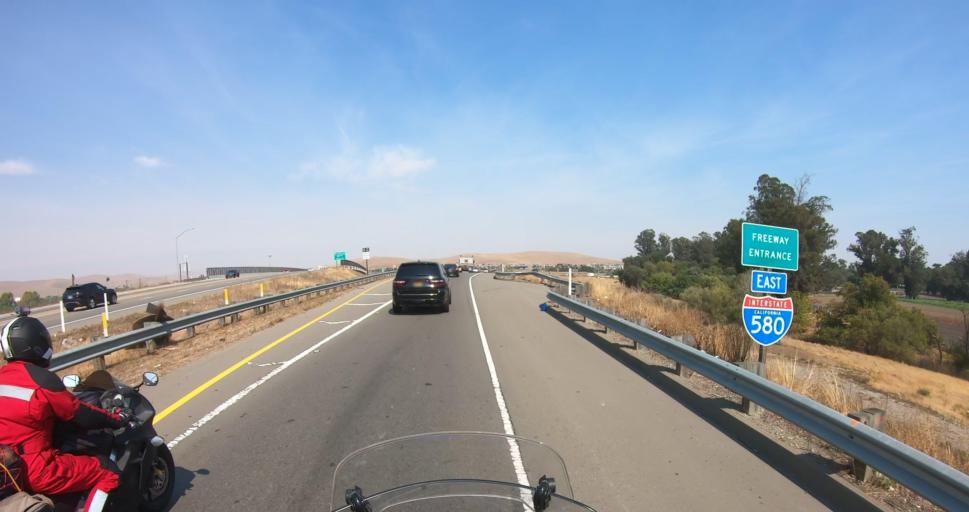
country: US
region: California
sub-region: Alameda County
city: Livermore
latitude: 37.6992
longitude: -121.8026
